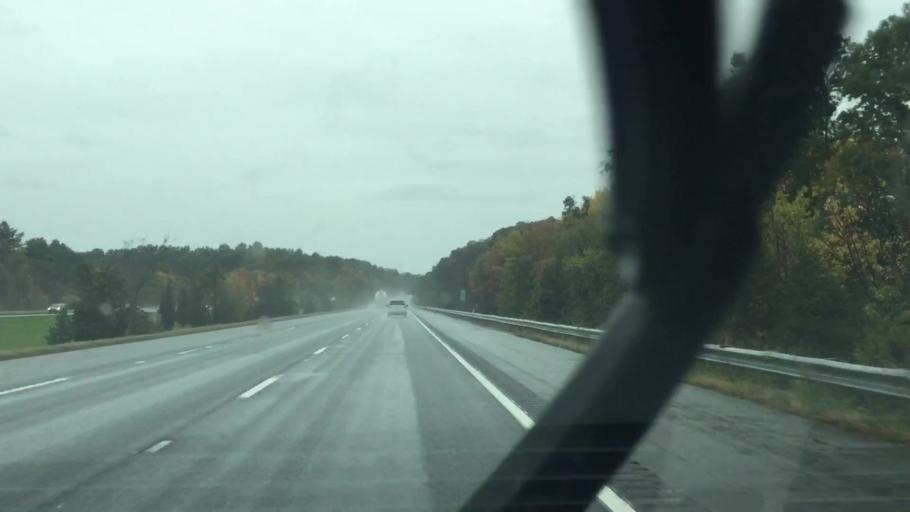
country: US
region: Massachusetts
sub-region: Essex County
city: Merrimac
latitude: 42.8118
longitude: -71.0265
